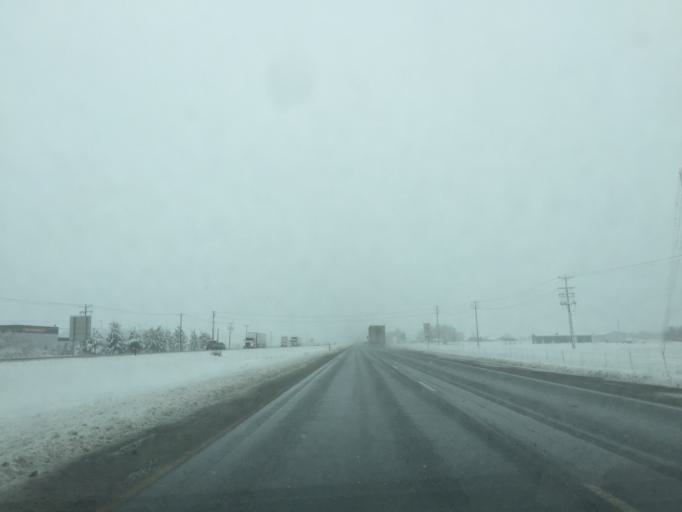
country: US
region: Washington
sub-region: Spokane County
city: Airway Heights
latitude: 47.5869
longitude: -117.5704
